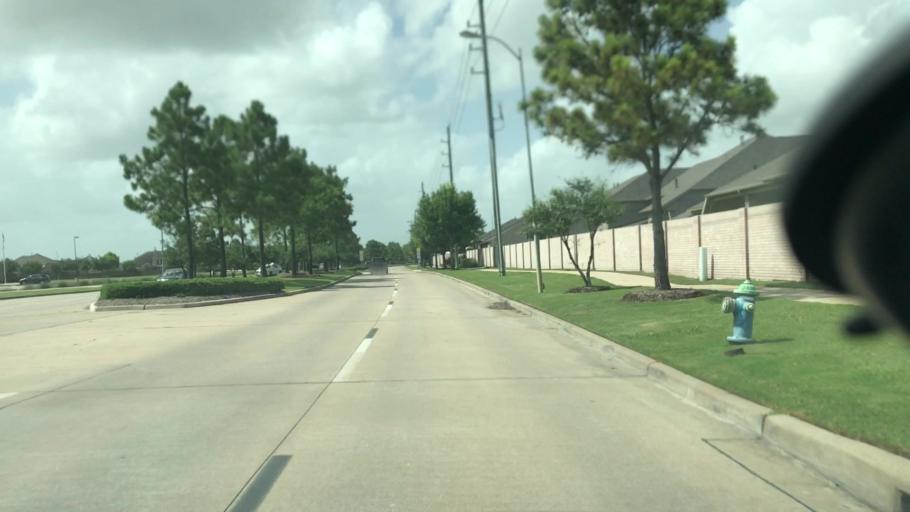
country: US
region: Texas
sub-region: Fort Bend County
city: Fresno
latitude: 29.5598
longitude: -95.4173
